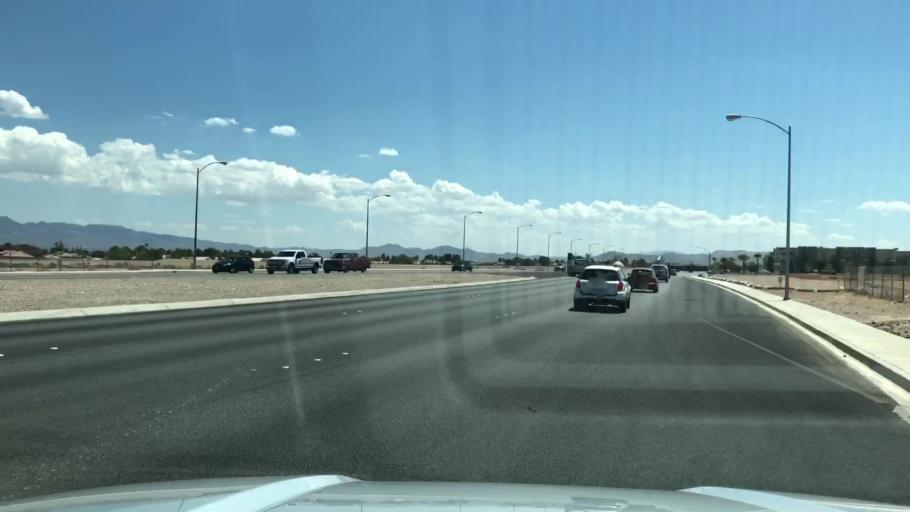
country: US
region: Nevada
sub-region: Clark County
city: Enterprise
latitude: 36.0666
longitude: -115.2081
